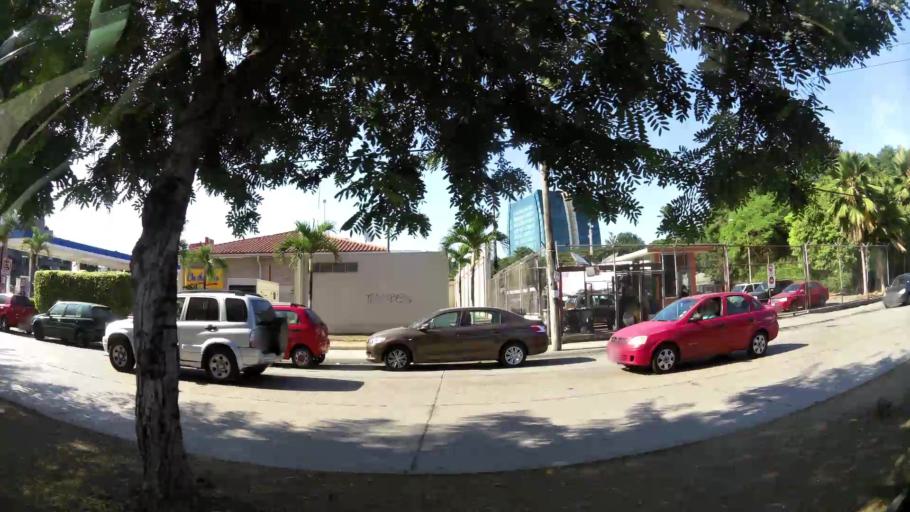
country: EC
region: Guayas
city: Guayaquil
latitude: -2.1647
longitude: -79.8974
